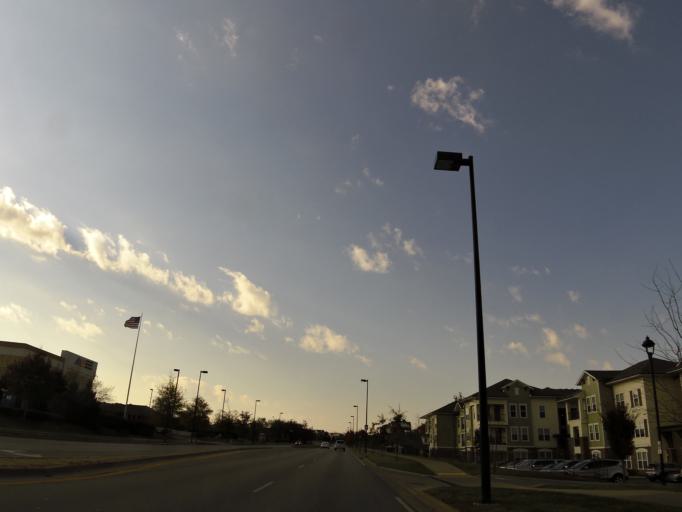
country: US
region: Kentucky
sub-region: Fayette County
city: Lexington-Fayette
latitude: 38.0280
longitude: -84.4214
